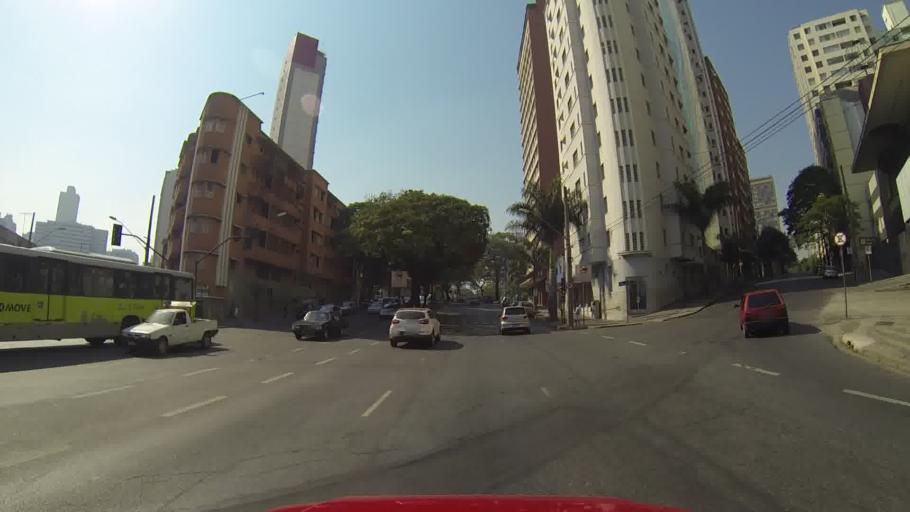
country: BR
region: Minas Gerais
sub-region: Belo Horizonte
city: Belo Horizonte
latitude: -19.9214
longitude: -43.9461
